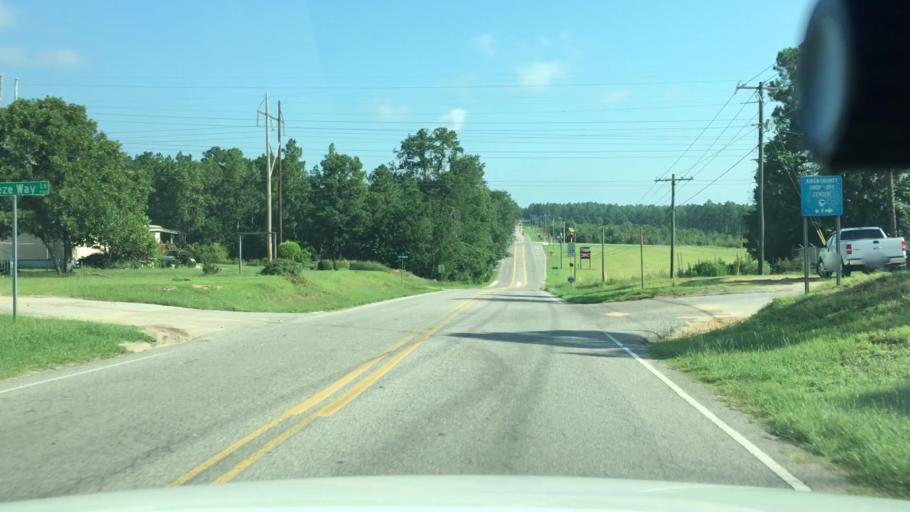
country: US
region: South Carolina
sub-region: Aiken County
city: Graniteville
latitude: 33.5805
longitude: -81.8360
